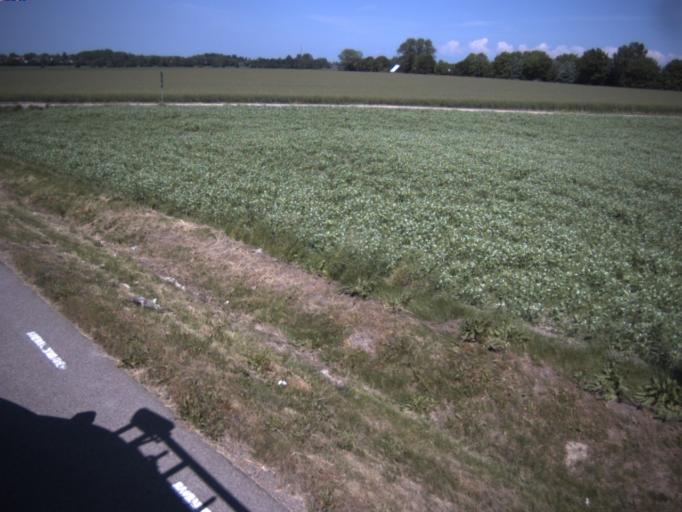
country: SE
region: Skane
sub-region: Helsingborg
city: Barslov
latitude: 56.0160
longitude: 12.8079
